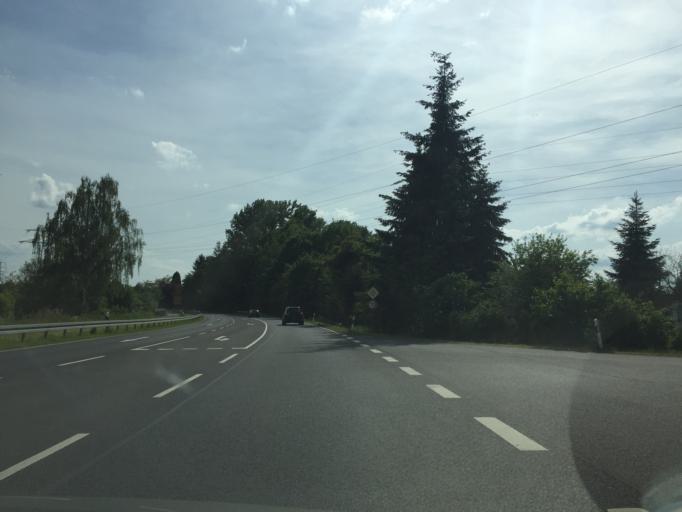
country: DE
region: Bavaria
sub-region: Regierungsbezirk Unterfranken
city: Kahl am Main
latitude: 50.0447
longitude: 9.0456
